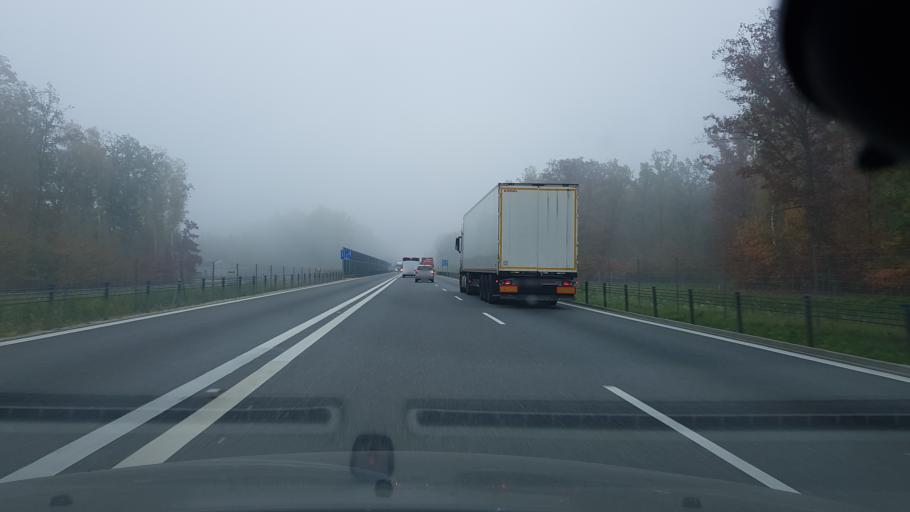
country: PL
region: Masovian Voivodeship
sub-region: Powiat zyrardowski
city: Wiskitki
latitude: 52.0660
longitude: 20.3863
